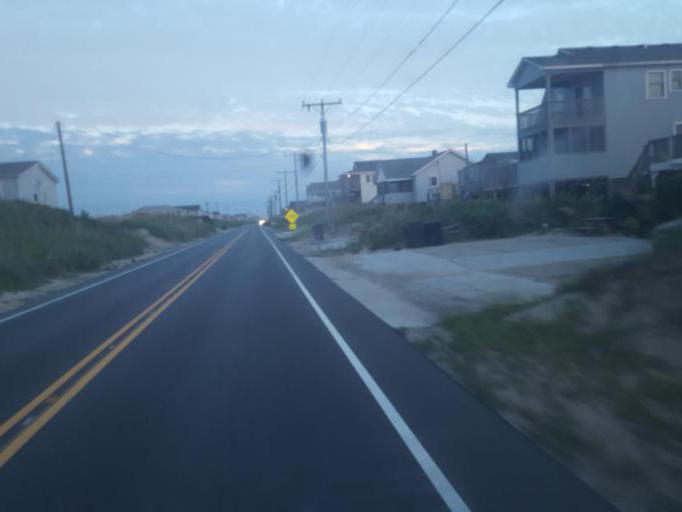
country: US
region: North Carolina
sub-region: Dare County
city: Kill Devil Hills
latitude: 36.0548
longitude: -75.6824
